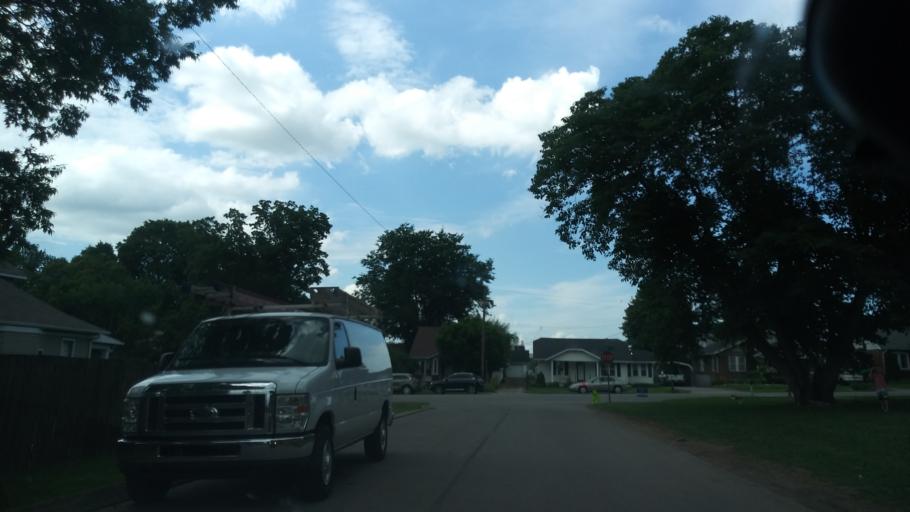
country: US
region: Tennessee
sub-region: Davidson County
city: Belle Meade
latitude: 36.1507
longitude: -86.8408
